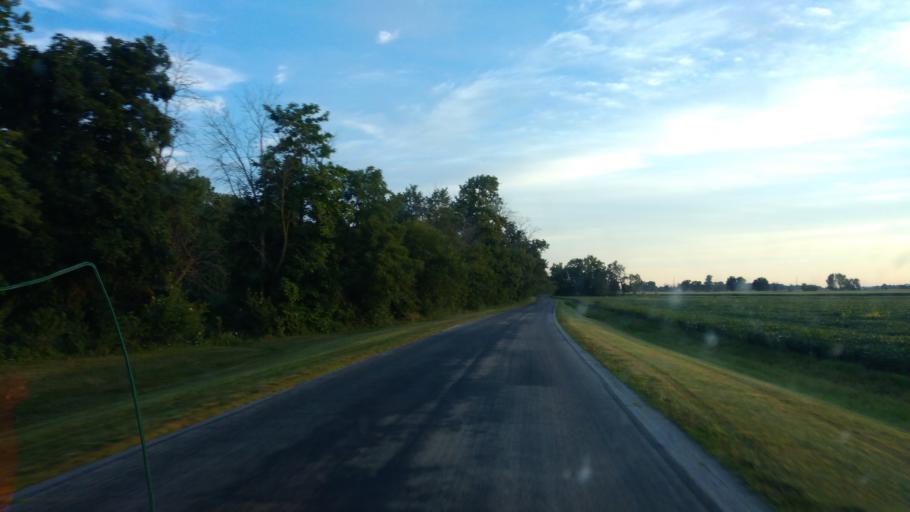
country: US
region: Indiana
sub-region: Adams County
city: Berne
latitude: 40.6498
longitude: -85.0309
